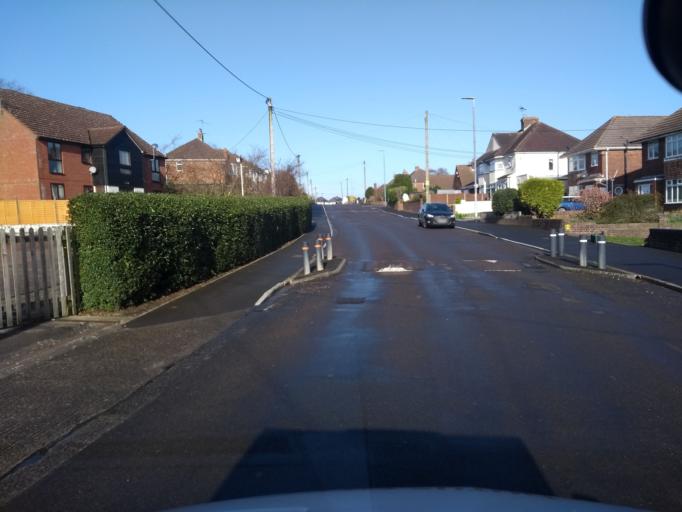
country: GB
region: England
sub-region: Somerset
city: Yeovil
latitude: 50.9558
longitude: -2.6274
